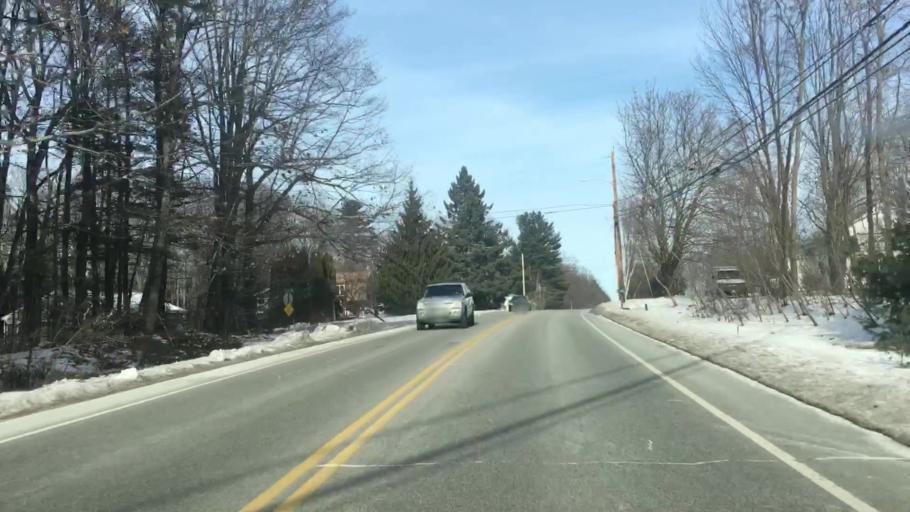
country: US
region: Maine
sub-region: Cumberland County
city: South Windham
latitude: 43.7698
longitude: -70.4207
